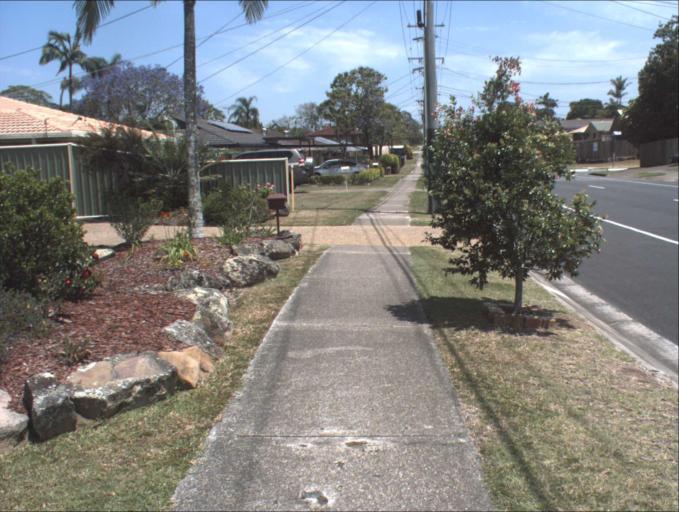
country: AU
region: Queensland
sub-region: Logan
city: Slacks Creek
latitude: -27.6389
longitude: 153.1459
